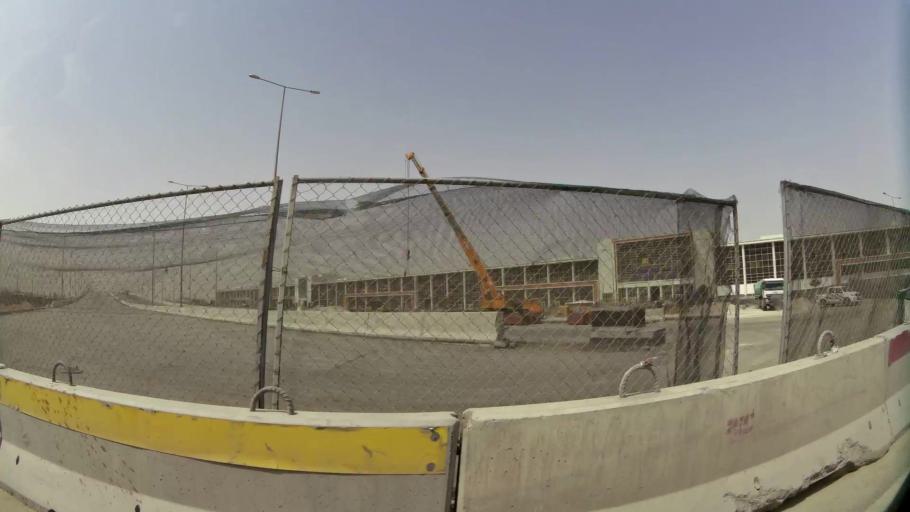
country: QA
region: Al Wakrah
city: Al Wukayr
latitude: 25.1946
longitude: 51.4603
